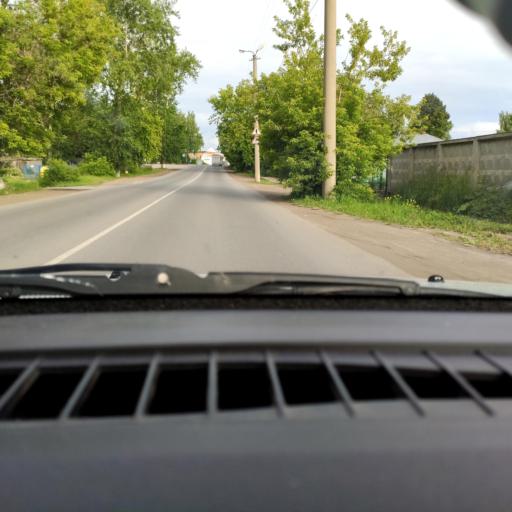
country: RU
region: Perm
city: Kungur
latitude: 57.4237
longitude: 56.9563
